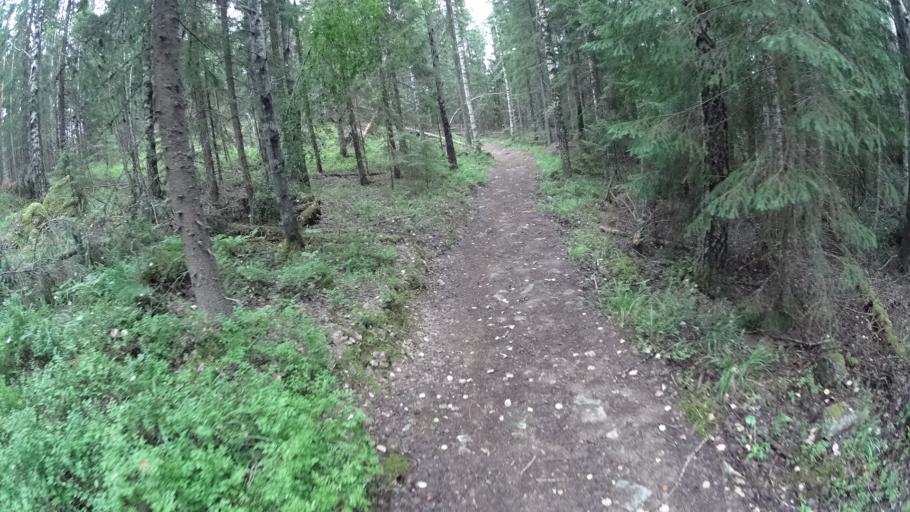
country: FI
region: Southern Savonia
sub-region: Mikkeli
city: Maentyharju
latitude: 61.1820
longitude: 26.8881
